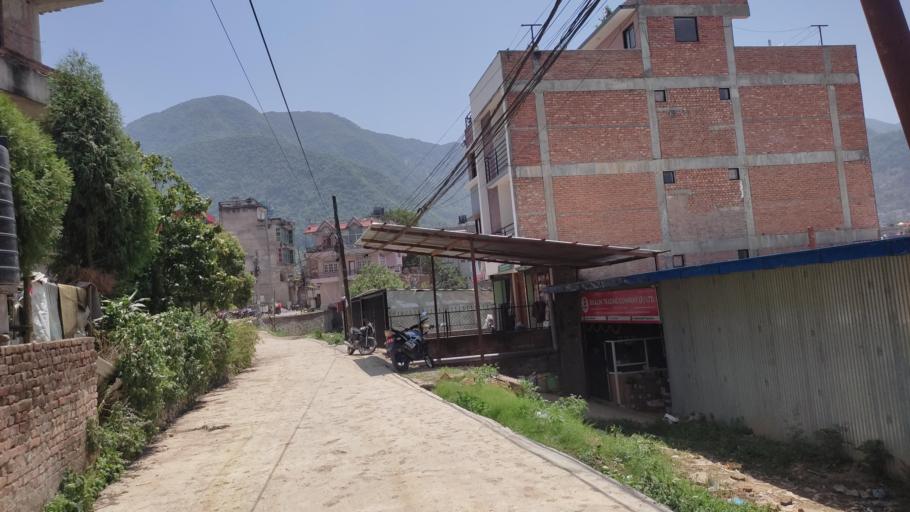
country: NP
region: Central Region
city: Kirtipur
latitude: 27.6678
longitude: 85.2669
